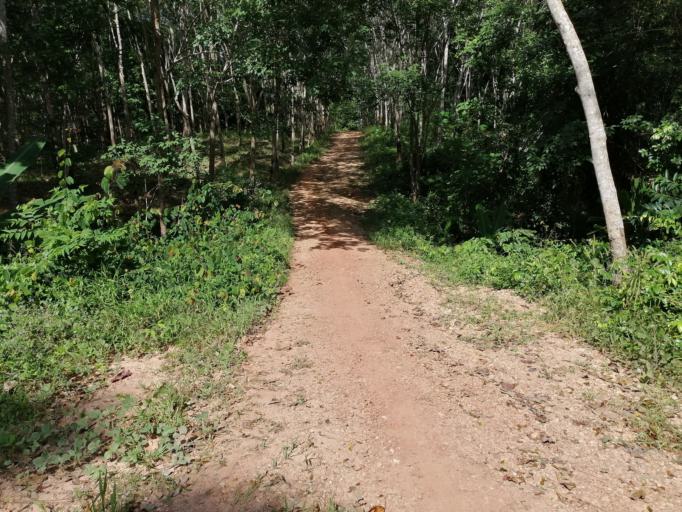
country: TH
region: Trang
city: Sikao
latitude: 7.5809
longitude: 99.3687
